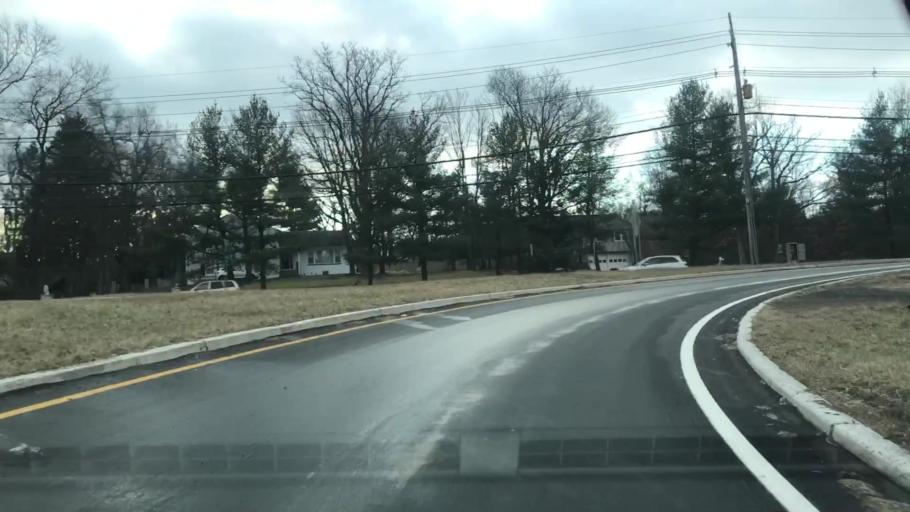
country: US
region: New Jersey
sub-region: Essex County
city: Roseland
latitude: 40.8079
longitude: -74.2859
